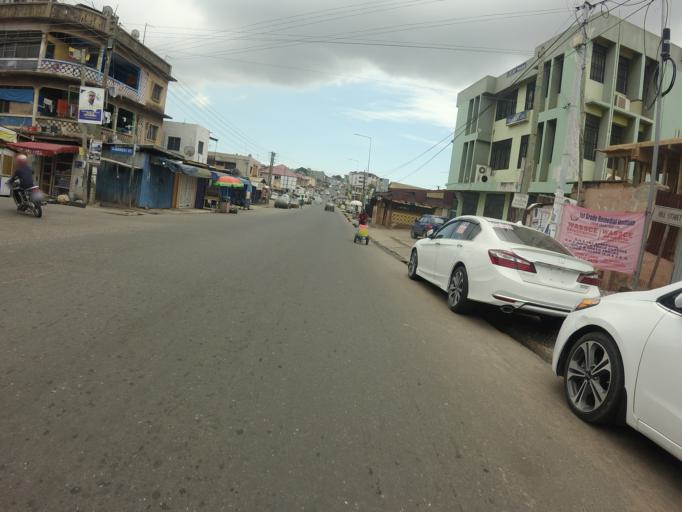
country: GH
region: Greater Accra
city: Accra
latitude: 5.5800
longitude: -0.2048
